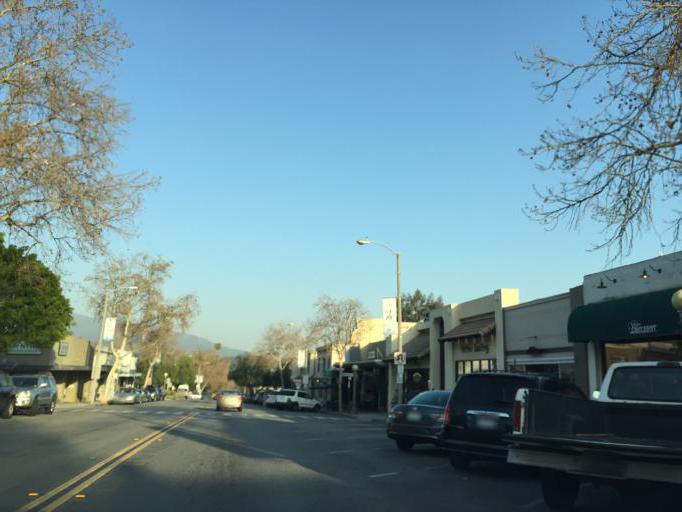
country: US
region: California
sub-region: Los Angeles County
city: Sierra Madre
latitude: 34.1619
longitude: -118.0545
